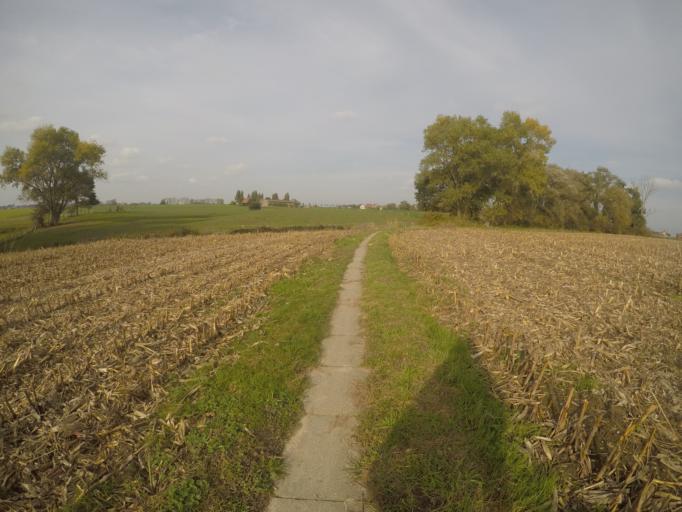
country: BE
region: Flanders
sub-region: Provincie West-Vlaanderen
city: Moorslede
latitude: 50.8347
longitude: 3.0578
